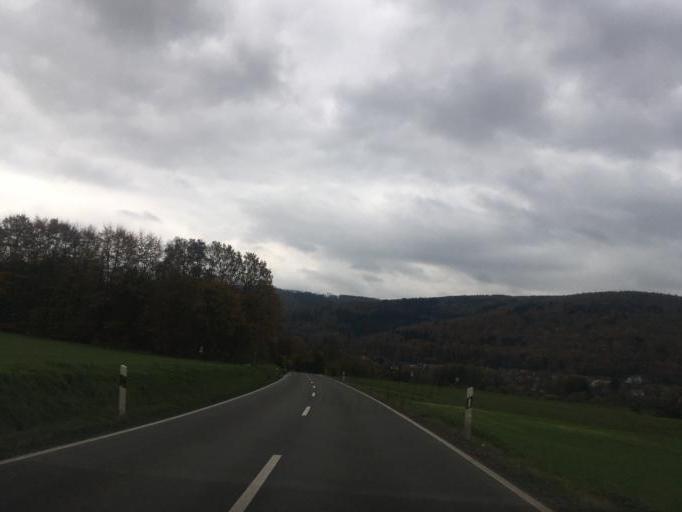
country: DE
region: Lower Saxony
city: Bodenfelde
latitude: 51.6070
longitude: 9.5496
